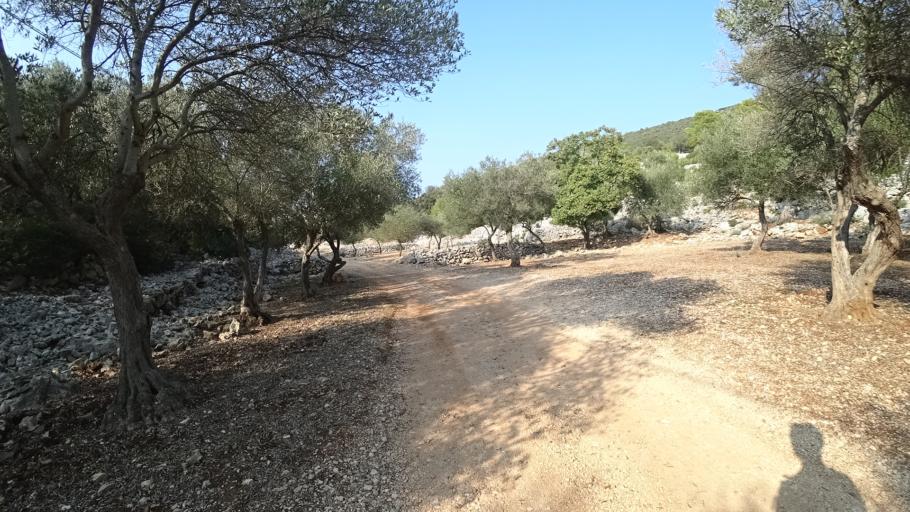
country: HR
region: Primorsko-Goranska
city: Mali Losinj
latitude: 44.4930
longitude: 14.5048
